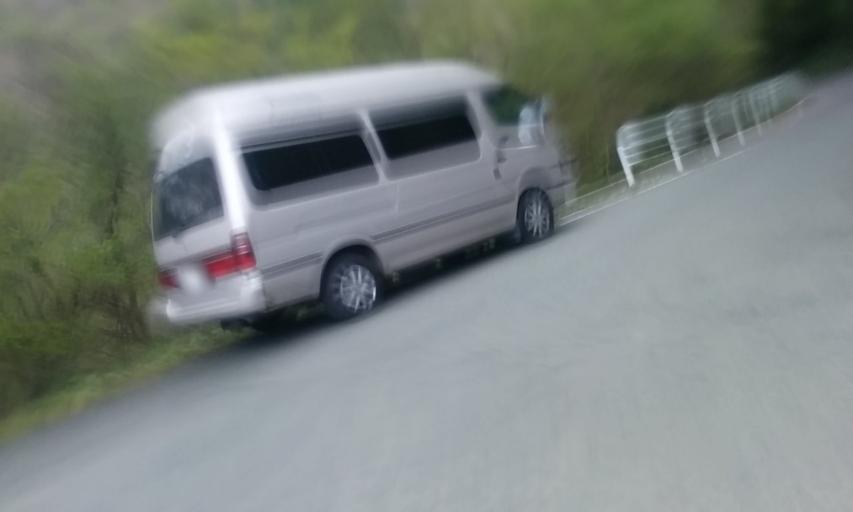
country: JP
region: Ehime
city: Saijo
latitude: 33.7990
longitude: 133.2669
